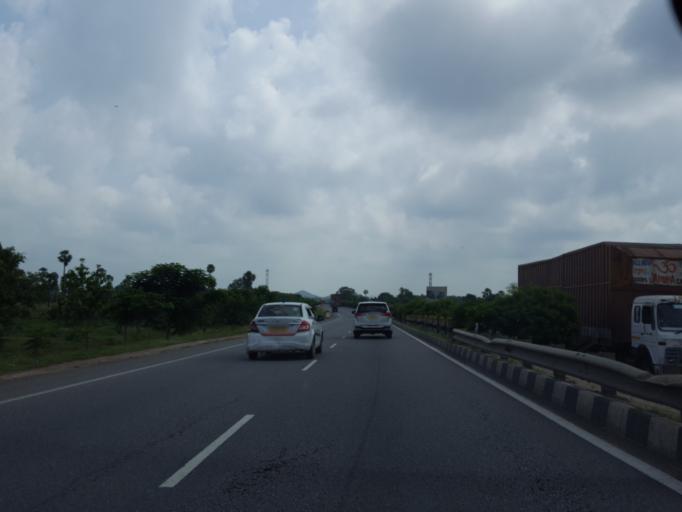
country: IN
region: Telangana
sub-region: Nalgonda
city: Bhongir
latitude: 17.2297
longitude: 79.0029
